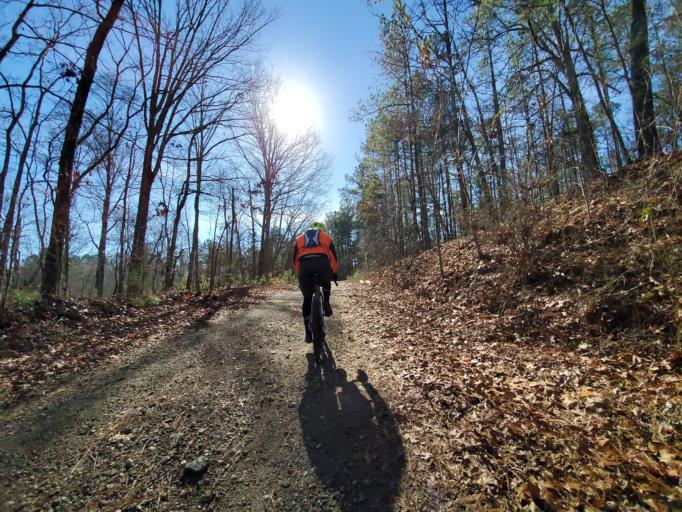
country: US
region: Georgia
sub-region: Fulton County
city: Chattahoochee Hills
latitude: 33.5683
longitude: -84.7537
